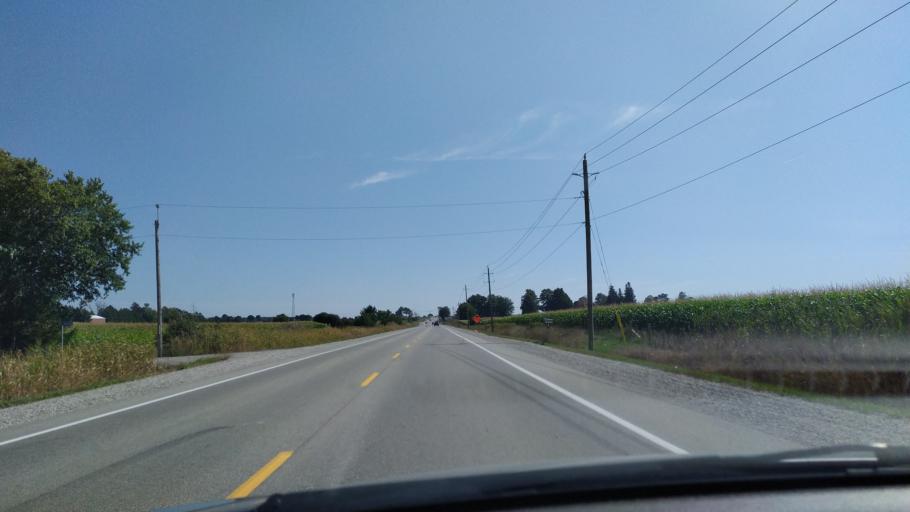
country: CA
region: Ontario
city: Ingersoll
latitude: 43.0585
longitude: -80.8322
